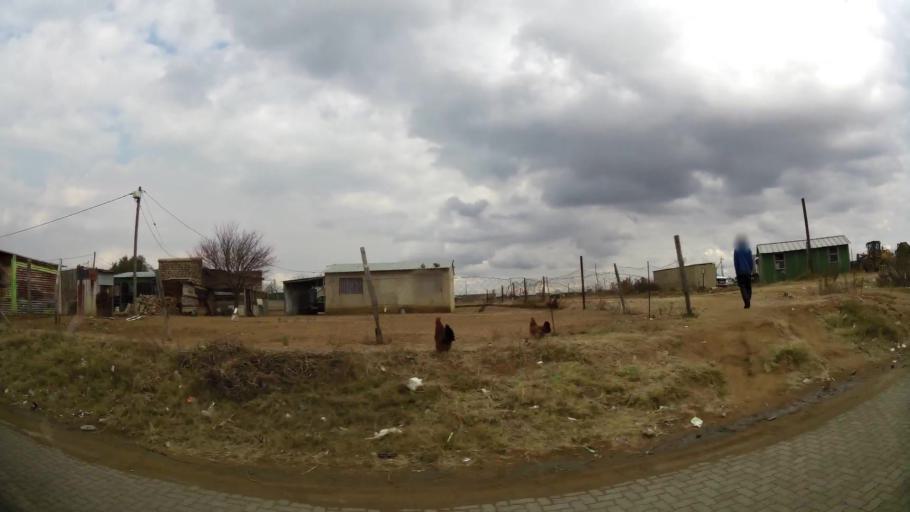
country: ZA
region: Orange Free State
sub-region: Fezile Dabi District Municipality
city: Sasolburg
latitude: -26.8688
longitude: 27.8714
